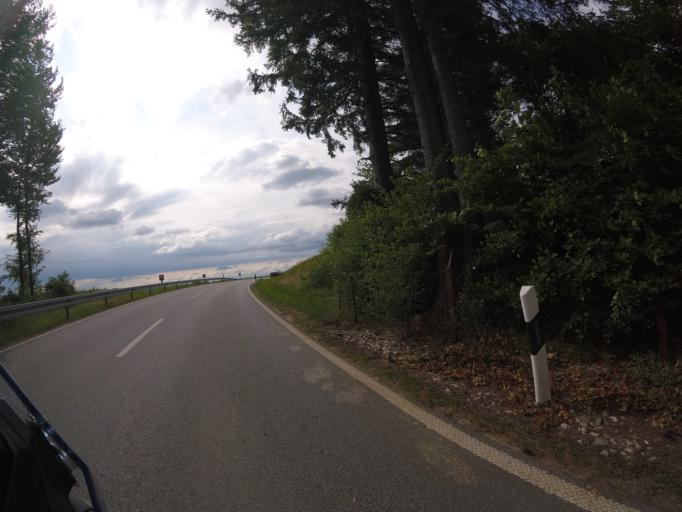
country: DE
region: Bavaria
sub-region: Upper Bavaria
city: Reichertshausen
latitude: 47.8824
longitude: 11.5209
